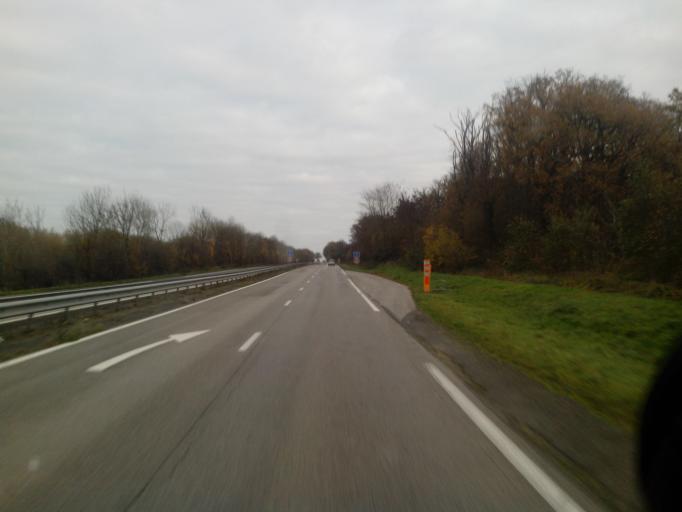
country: FR
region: Poitou-Charentes
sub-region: Departement des Deux-Sevres
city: La Peyratte
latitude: 46.6532
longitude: -0.1069
